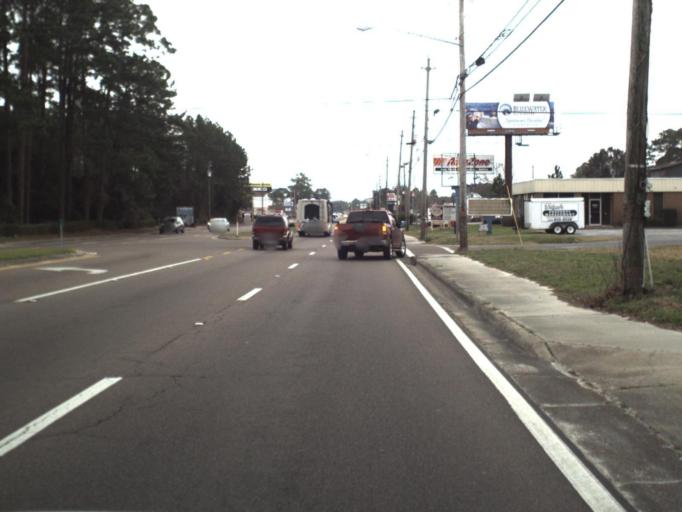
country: US
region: Florida
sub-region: Bay County
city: Parker
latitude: 30.1352
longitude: -85.5913
